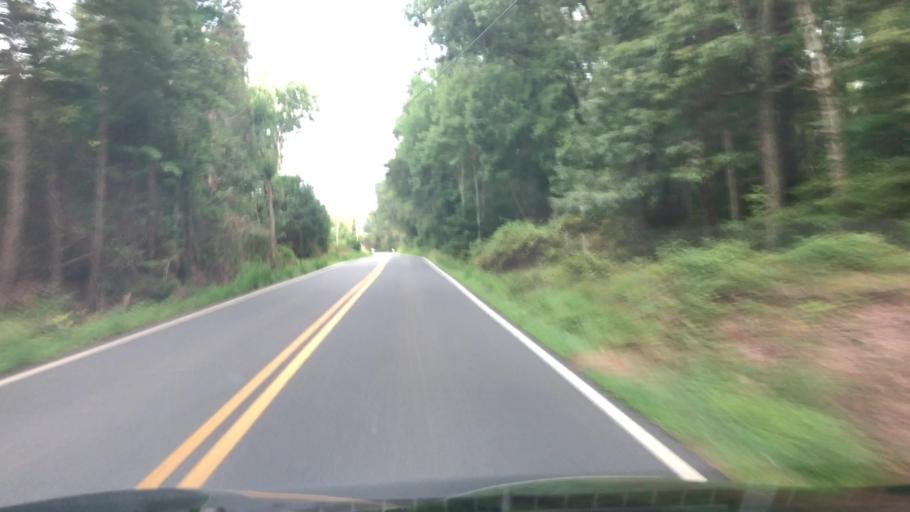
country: US
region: Virginia
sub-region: Fauquier County
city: Bealeton
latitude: 38.5431
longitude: -77.6765
